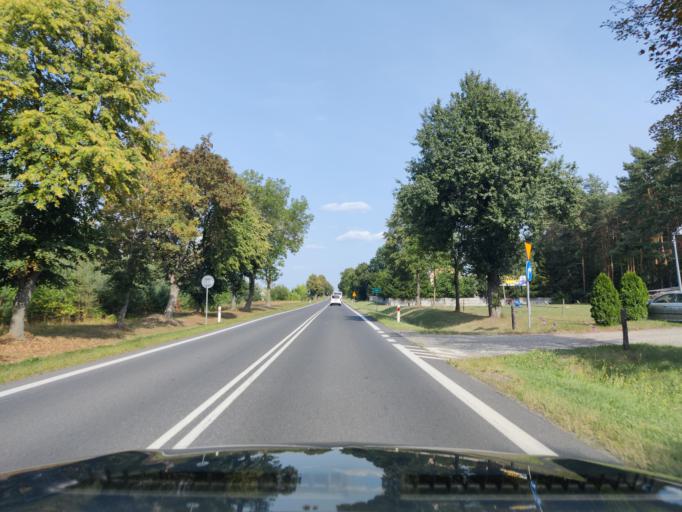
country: PL
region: Masovian Voivodeship
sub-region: Powiat makowski
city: Szelkow
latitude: 52.8399
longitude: 21.2570
